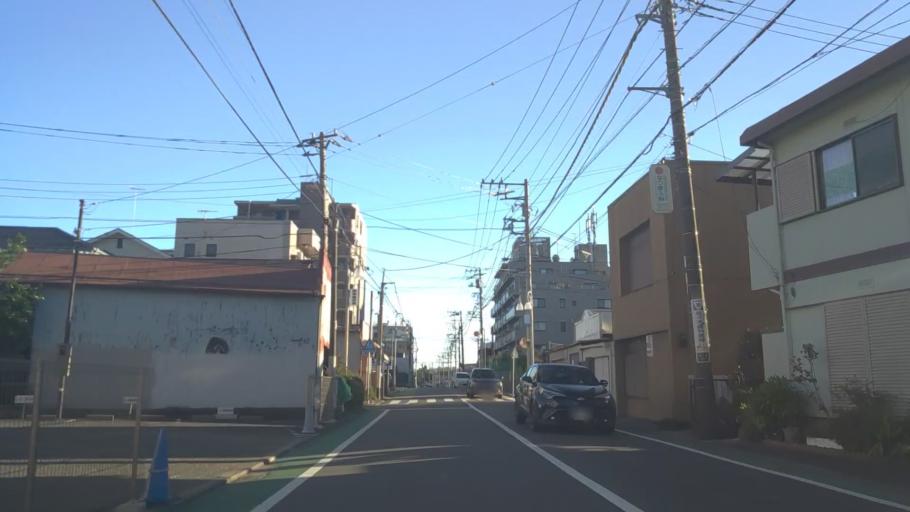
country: JP
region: Kanagawa
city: Chigasaki
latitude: 35.3319
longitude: 139.4147
